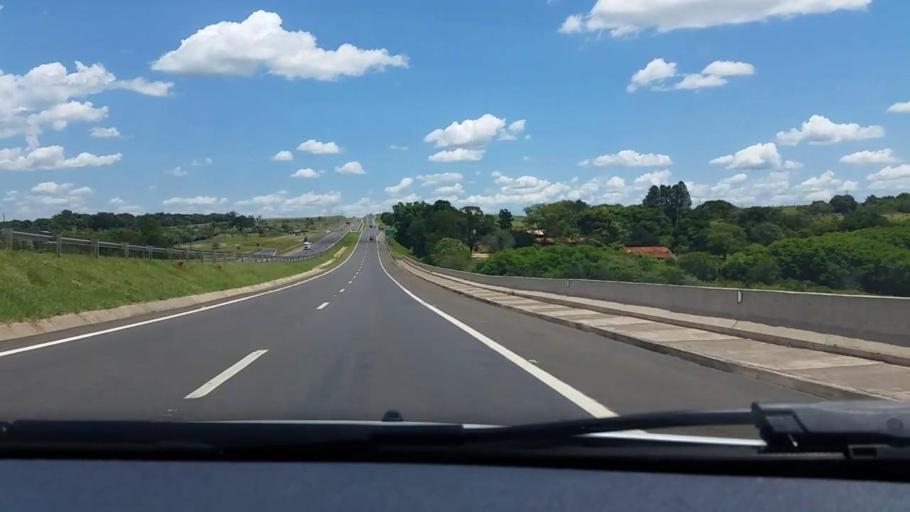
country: BR
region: Sao Paulo
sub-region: Bauru
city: Bauru
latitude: -22.3833
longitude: -49.0684
